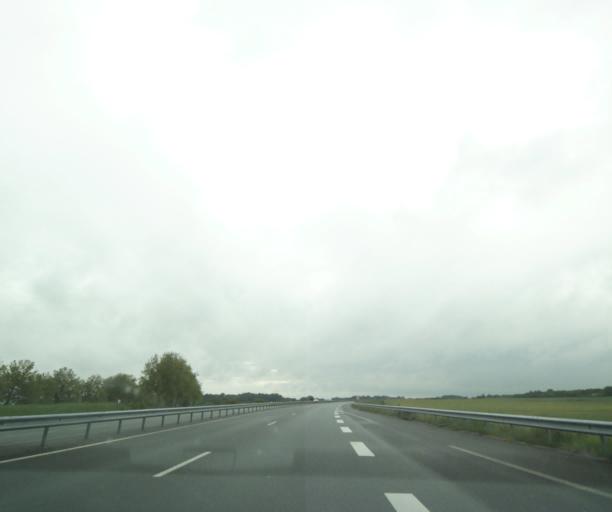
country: FR
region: Poitou-Charentes
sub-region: Departement de la Charente-Maritime
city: Corme-Royal
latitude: 45.7046
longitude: -0.7664
